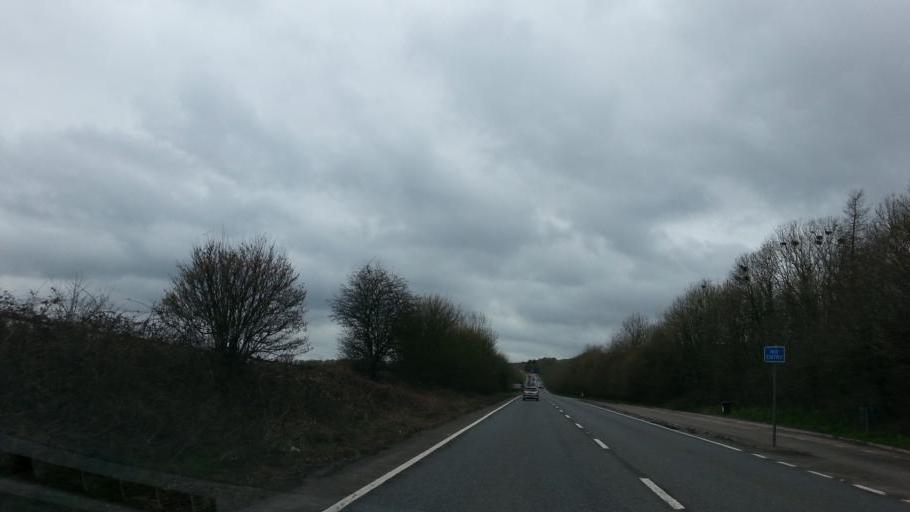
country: GB
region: England
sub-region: Devon
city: South Molton
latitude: 51.0348
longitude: -3.8460
